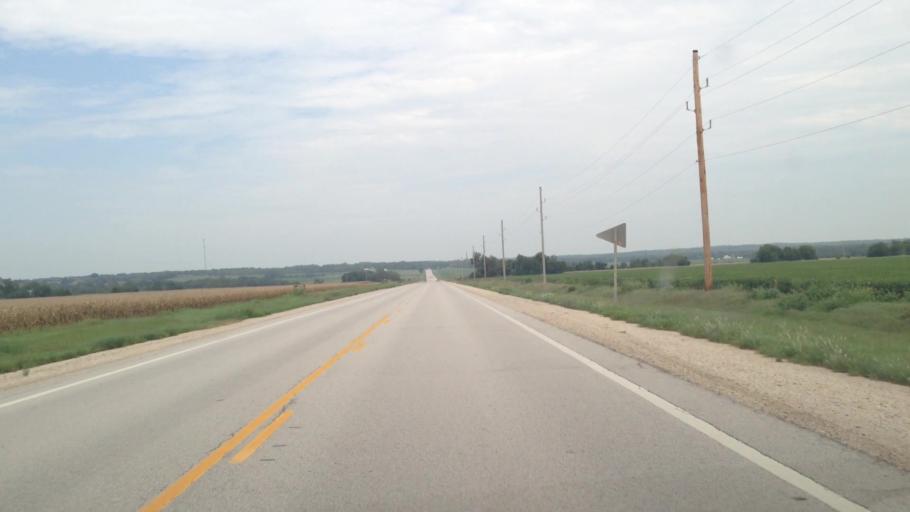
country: US
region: Kansas
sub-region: Anderson County
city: Garnett
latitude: 38.0581
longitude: -95.1694
